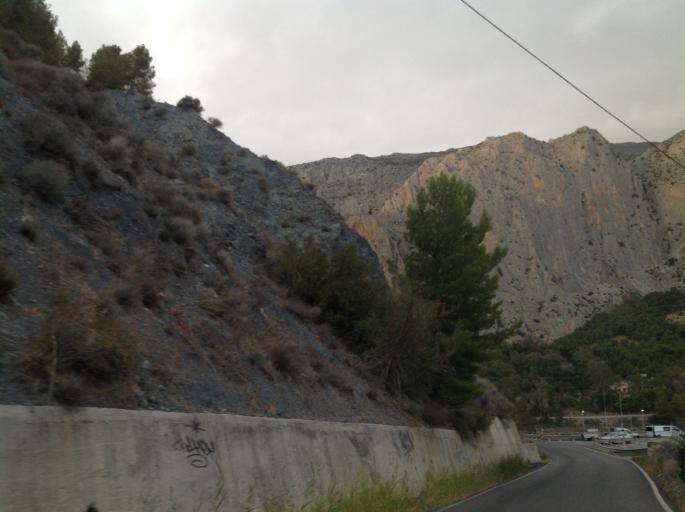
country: ES
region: Andalusia
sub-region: Provincia de Malaga
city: Carratraca
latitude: 36.9074
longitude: -4.7644
